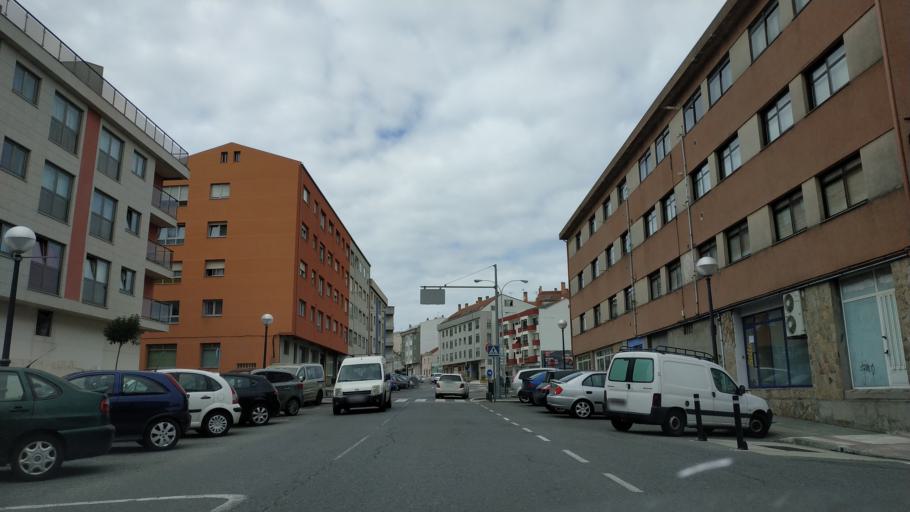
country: ES
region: Galicia
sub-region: Provincia da Coruna
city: Arteixo
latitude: 43.3033
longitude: -8.5139
